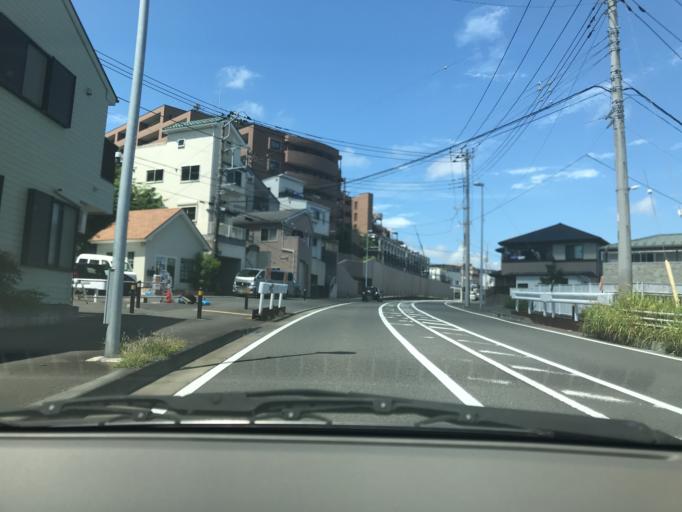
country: JP
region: Kanagawa
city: Fujisawa
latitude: 35.3621
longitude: 139.4629
